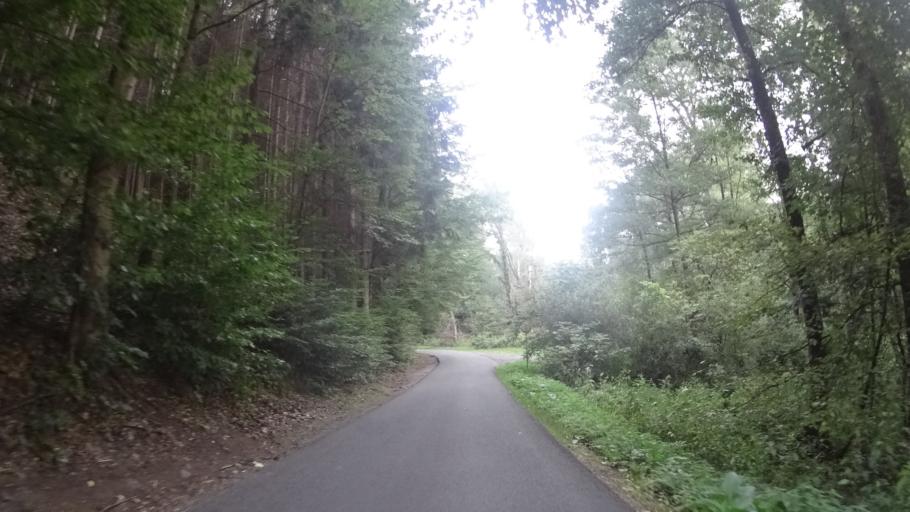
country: CZ
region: Olomoucky
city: Zabreh
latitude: 49.8692
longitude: 16.7887
